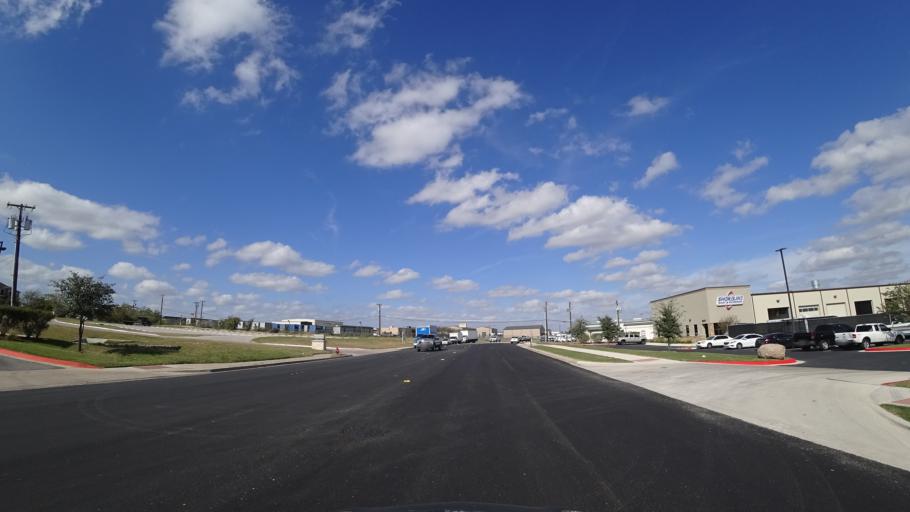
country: US
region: Texas
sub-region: Travis County
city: Windemere
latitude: 30.4569
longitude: -97.6601
